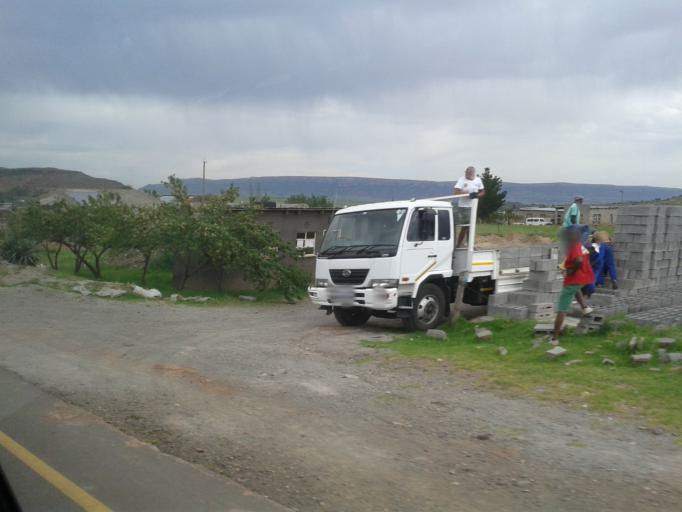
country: LS
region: Maseru
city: Maseru
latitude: -29.4140
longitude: 27.6305
